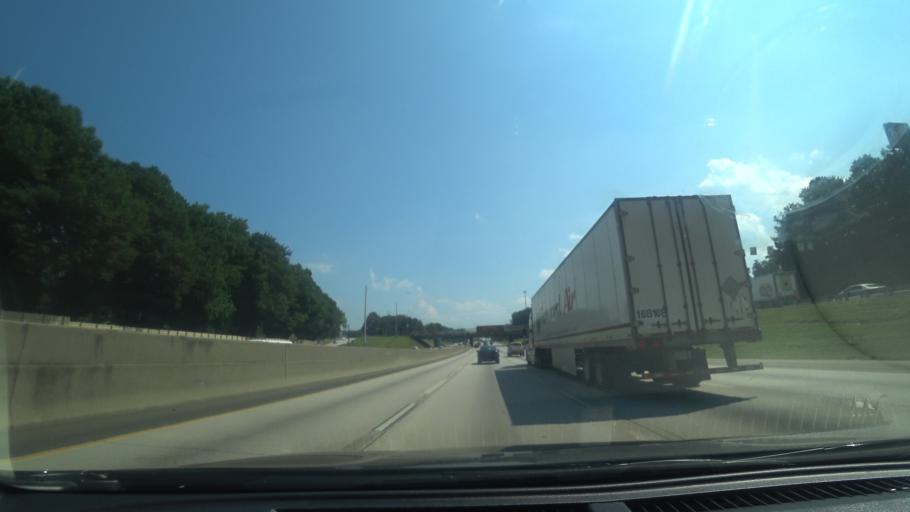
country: US
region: Georgia
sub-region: DeKalb County
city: Belvedere Park
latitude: 33.7548
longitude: -84.2324
